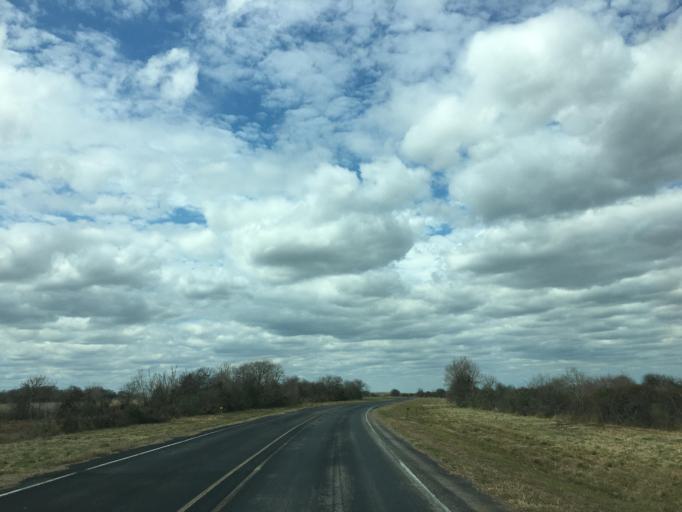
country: US
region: Texas
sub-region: Brazoria County
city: Oyster Creek
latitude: 29.0594
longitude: -95.2760
